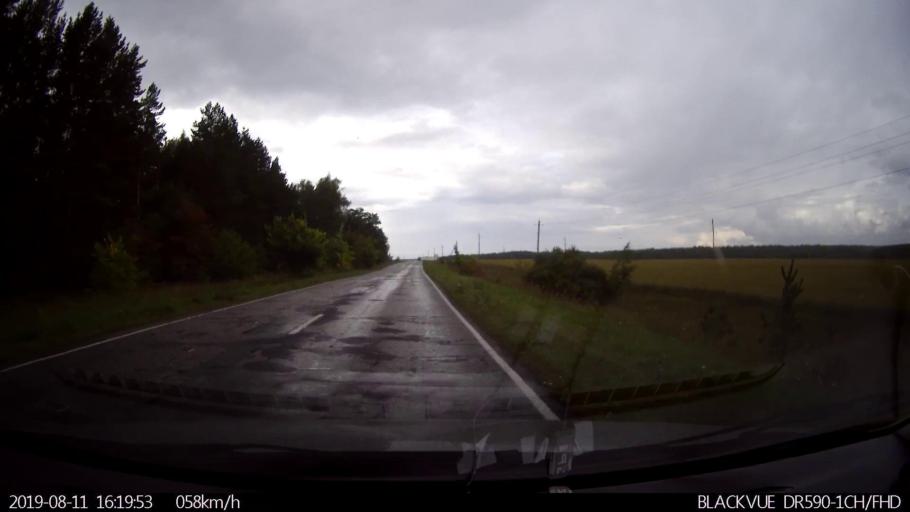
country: RU
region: Ulyanovsk
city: Mayna
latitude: 54.0675
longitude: 47.6053
